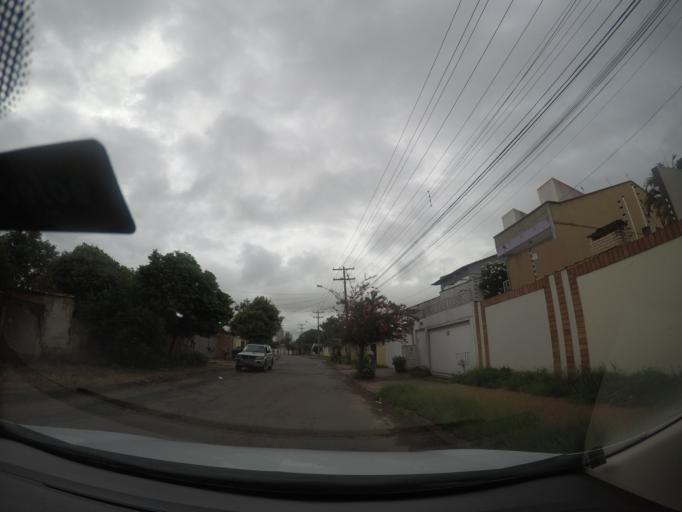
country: BR
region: Goias
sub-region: Goiania
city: Goiania
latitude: -16.7221
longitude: -49.2918
